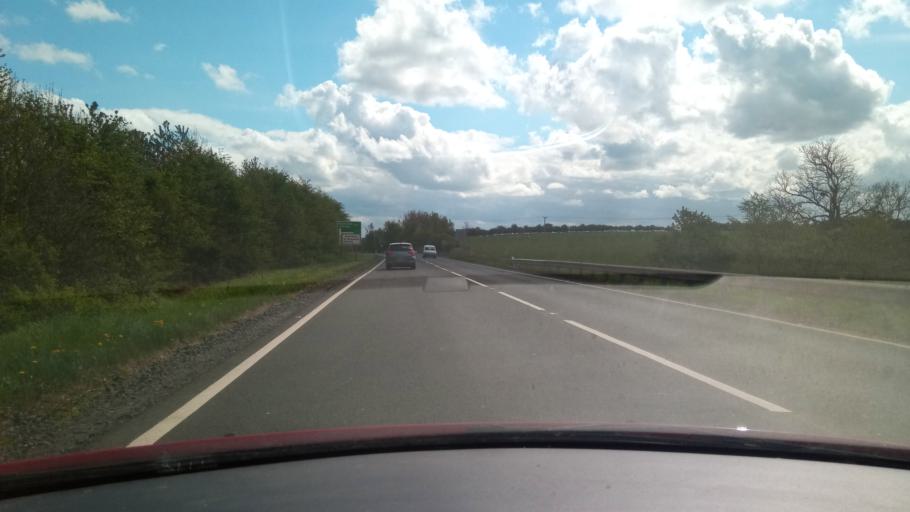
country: GB
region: Scotland
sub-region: The Scottish Borders
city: Newtown St Boswells
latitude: 55.5868
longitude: -2.6725
